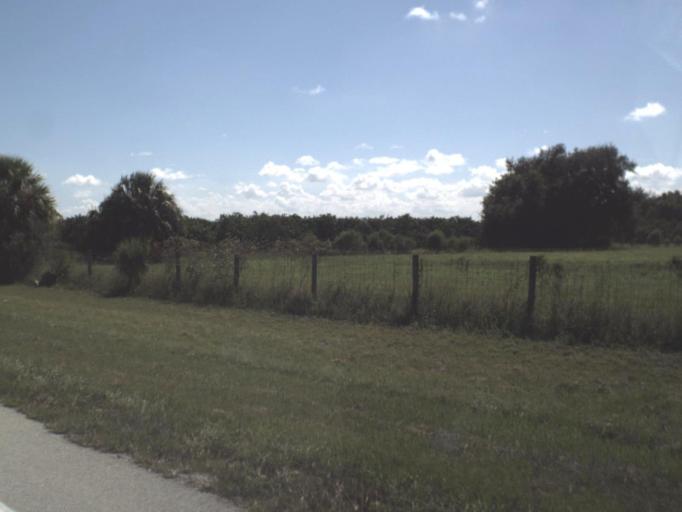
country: US
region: Florida
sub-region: Hendry County
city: Port LaBelle
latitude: 26.8128
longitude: -81.3511
